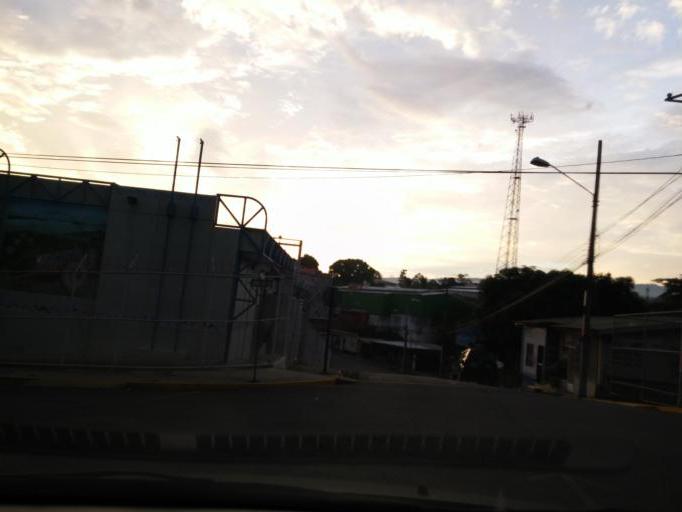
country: CR
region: Alajuela
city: San Juan
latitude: 10.0901
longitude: -84.3455
